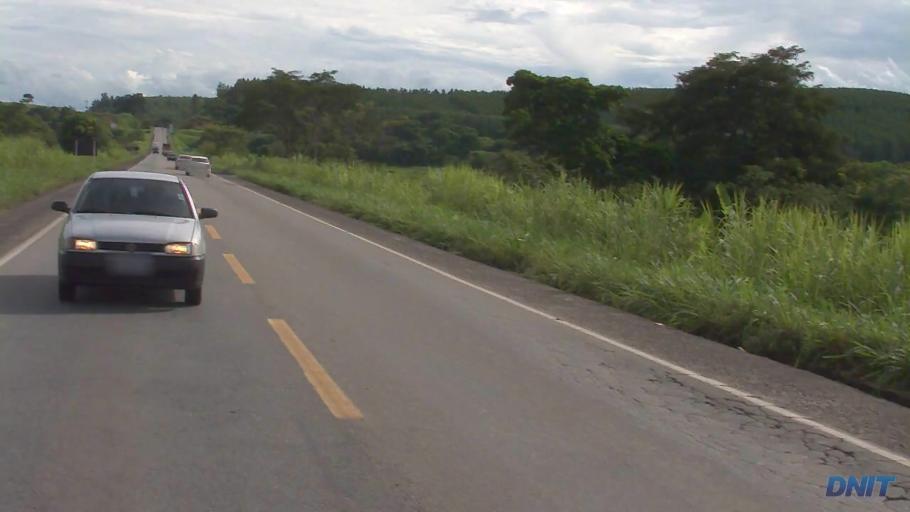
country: BR
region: Minas Gerais
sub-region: Belo Oriente
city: Belo Oriente
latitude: -19.2396
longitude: -42.3335
